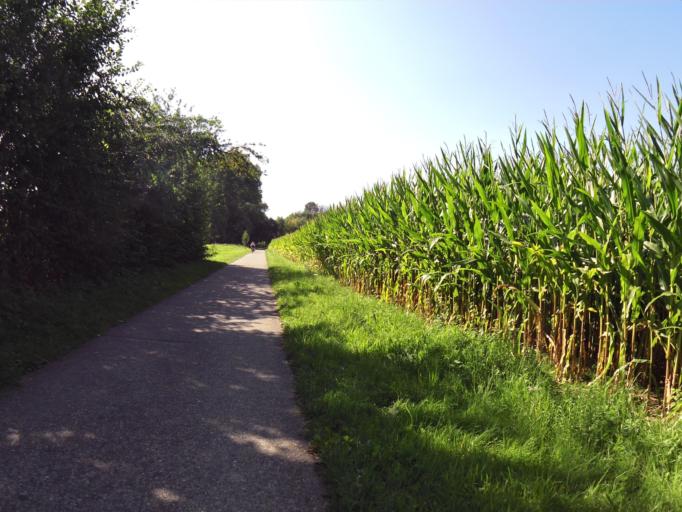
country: BE
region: Flanders
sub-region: Provincie Limburg
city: Tongeren
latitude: 50.7766
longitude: 5.4955
